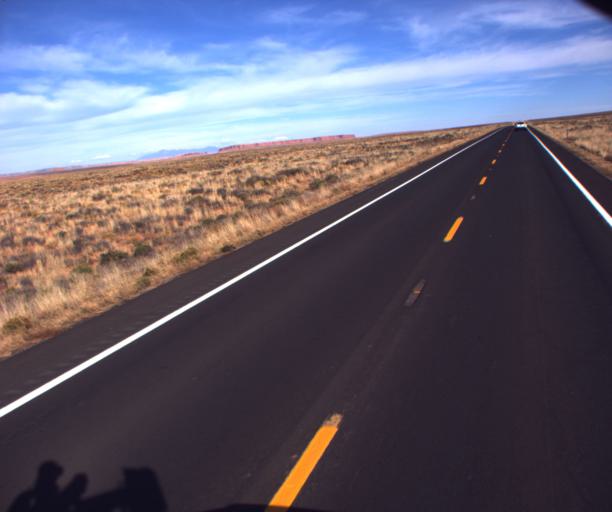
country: US
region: Arizona
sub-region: Apache County
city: Lukachukai
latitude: 36.9638
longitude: -109.4745
